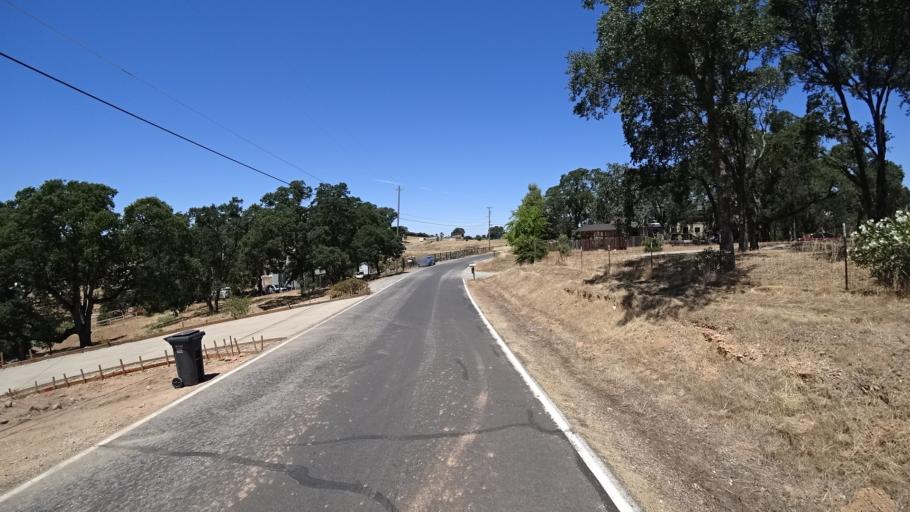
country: US
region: California
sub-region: Calaveras County
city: Rancho Calaveras
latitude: 38.1493
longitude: -120.8429
